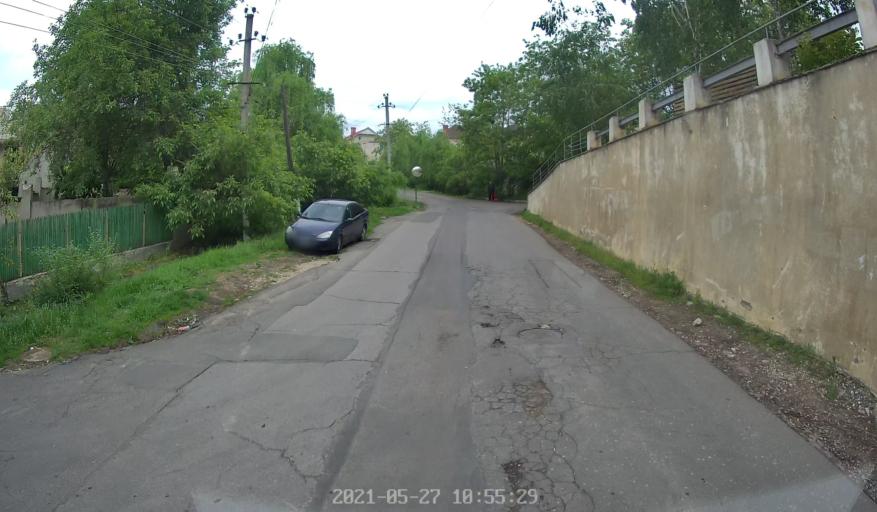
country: MD
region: Chisinau
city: Stauceni
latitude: 47.0959
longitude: 28.8672
